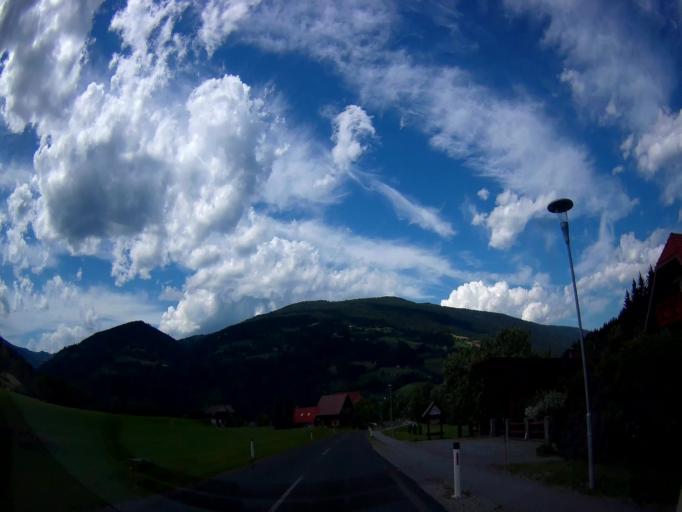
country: AT
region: Styria
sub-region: Politischer Bezirk Murau
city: Stadl an der Mur
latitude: 47.0764
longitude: 13.9829
